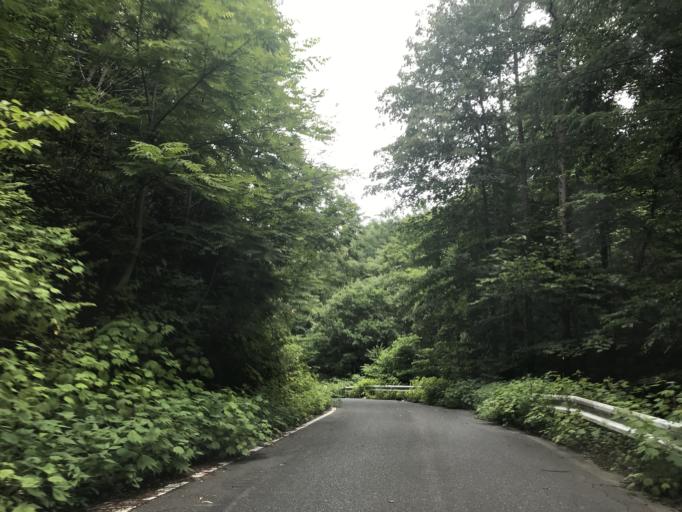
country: JP
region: Iwate
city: Ichinoseki
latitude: 38.9463
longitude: 140.8773
